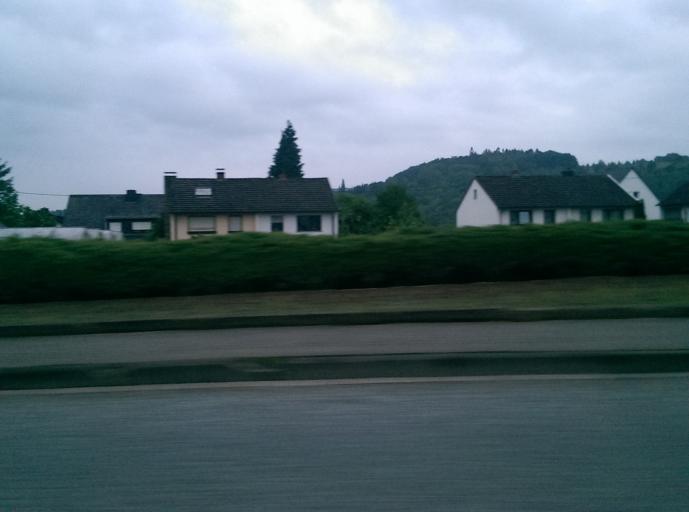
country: DE
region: Rheinland-Pfalz
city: Melsbach
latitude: 50.4676
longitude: 7.4737
